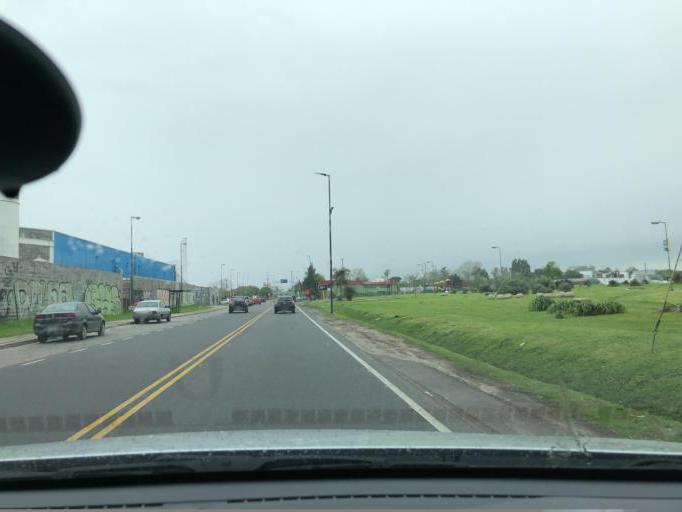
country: AR
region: Buenos Aires
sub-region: Partido de La Plata
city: La Plata
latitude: -34.8946
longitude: -57.9982
